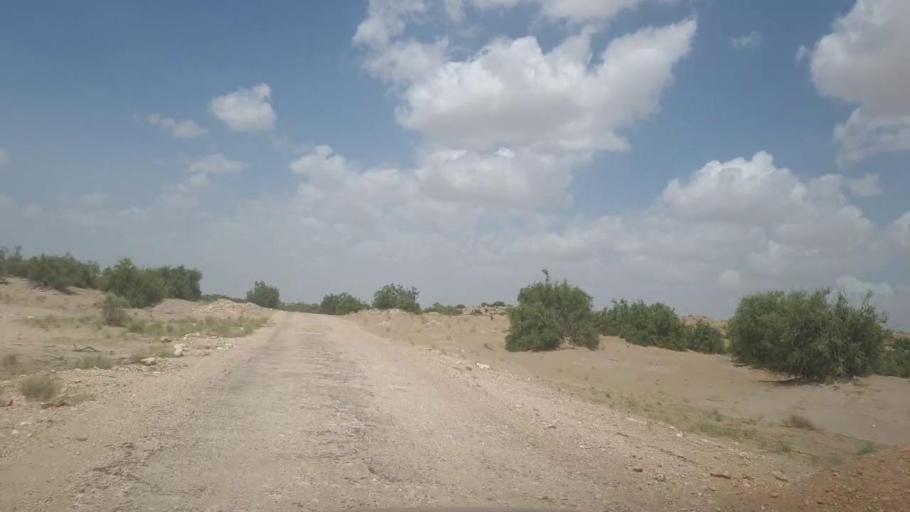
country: PK
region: Sindh
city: Kot Diji
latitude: 27.2564
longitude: 69.1679
